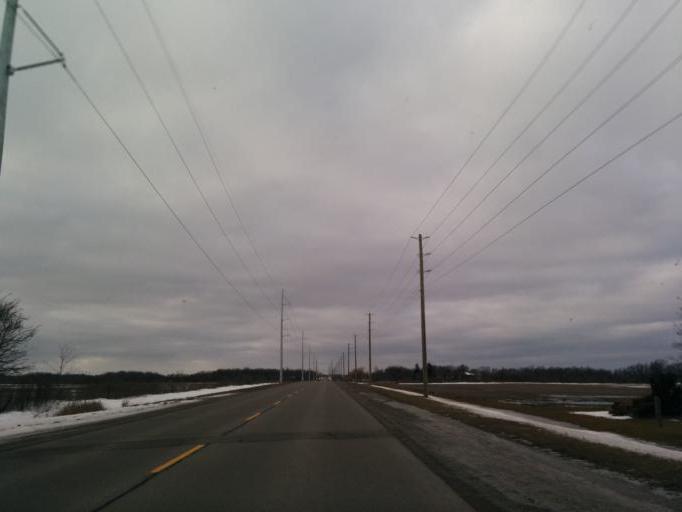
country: CA
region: Ontario
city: Ancaster
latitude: 42.9418
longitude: -79.9953
